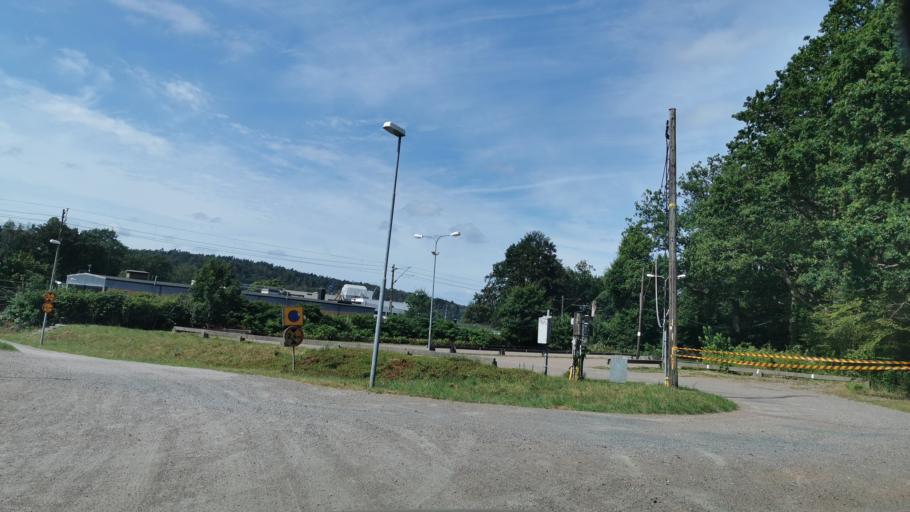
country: SE
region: Vaestra Goetaland
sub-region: Molndal
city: Moelndal
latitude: 57.6672
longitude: 12.0235
